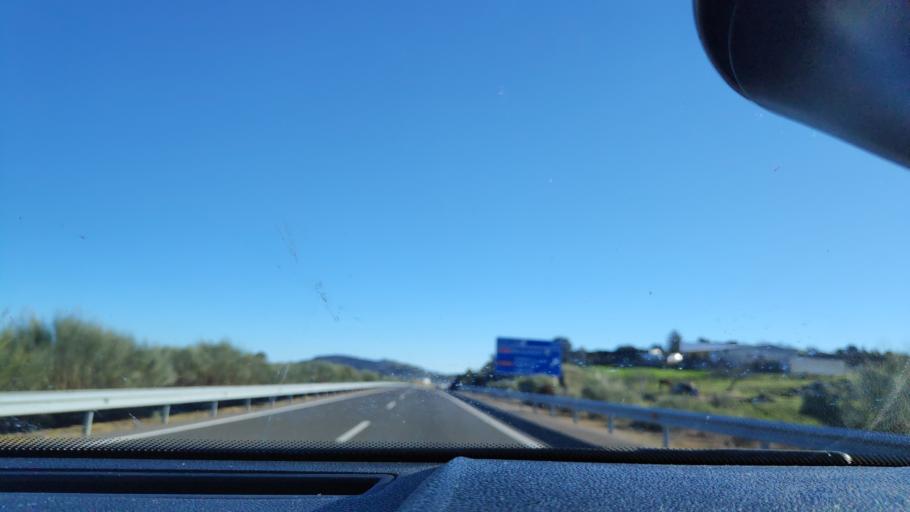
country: ES
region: Extremadura
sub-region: Provincia de Badajoz
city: Monesterio
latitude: 38.0971
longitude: -6.2676
